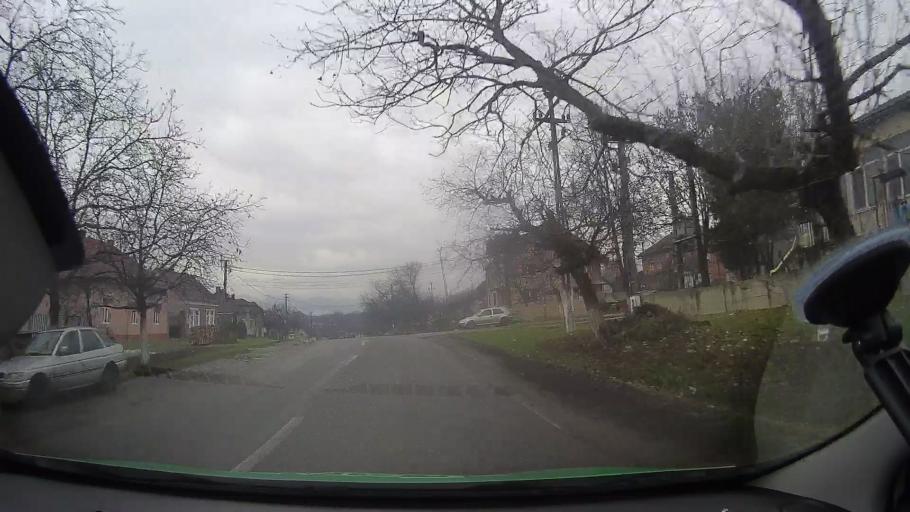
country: RO
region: Arad
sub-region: Comuna Gurahont
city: Gurahont
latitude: 46.2690
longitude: 22.3433
